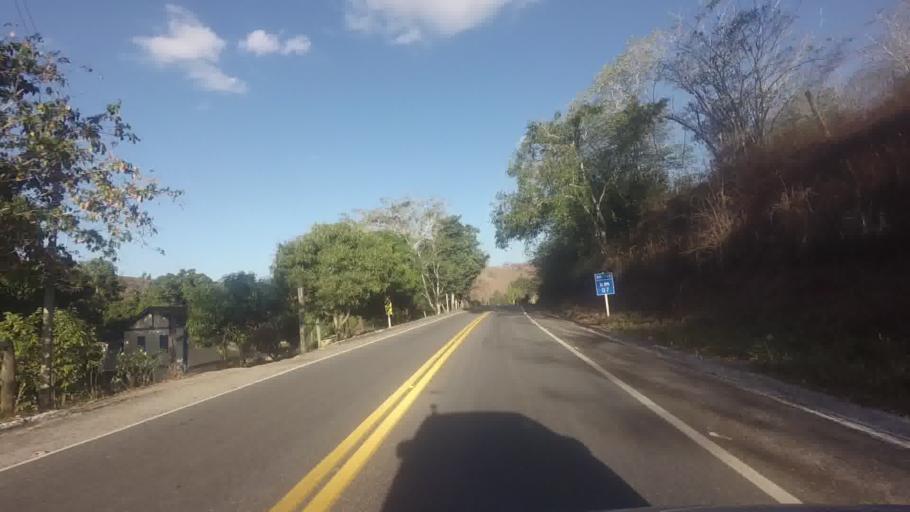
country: BR
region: Espirito Santo
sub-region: Cachoeiro De Itapemirim
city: Cachoeiro de Itapemirim
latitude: -20.8275
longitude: -41.2116
